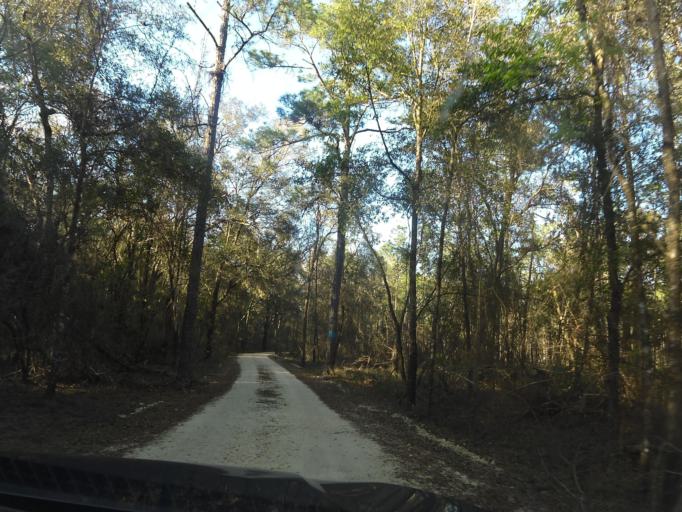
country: US
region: Florida
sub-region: Clay County
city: Middleburg
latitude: 30.1437
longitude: -81.9069
